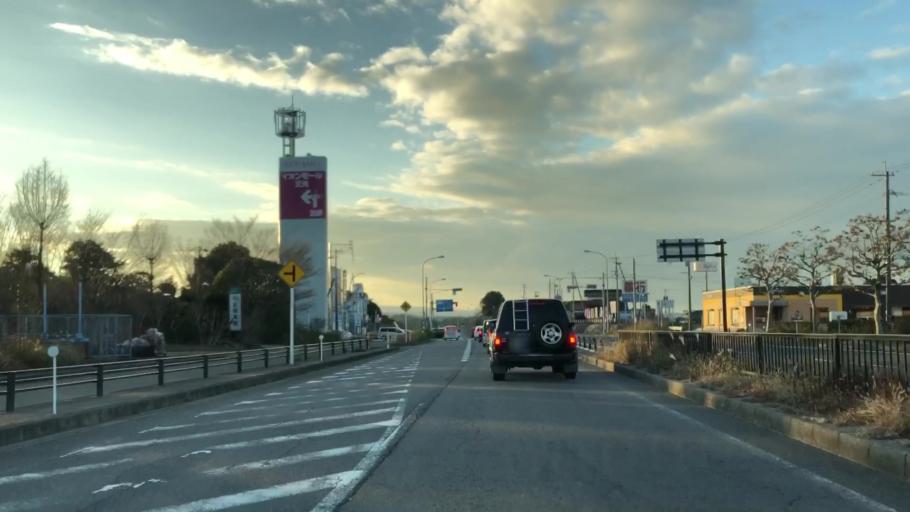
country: JP
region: Fukuoka
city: Nakatsu
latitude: 33.5602
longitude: 131.1959
